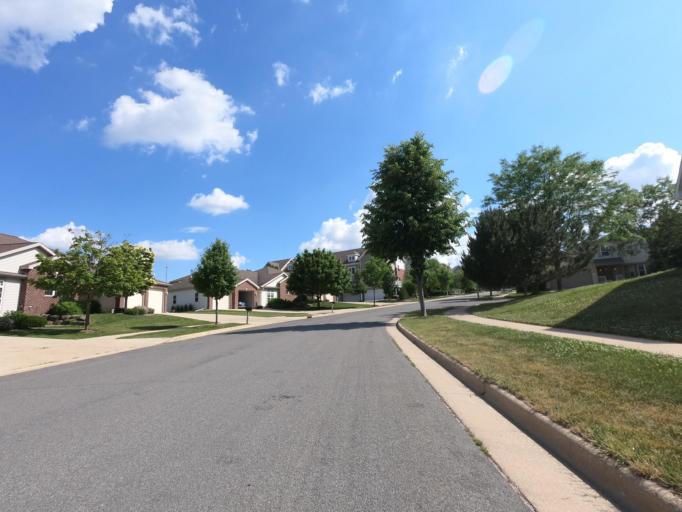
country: US
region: Wisconsin
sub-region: Dane County
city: Middleton
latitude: 43.0767
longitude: -89.5520
